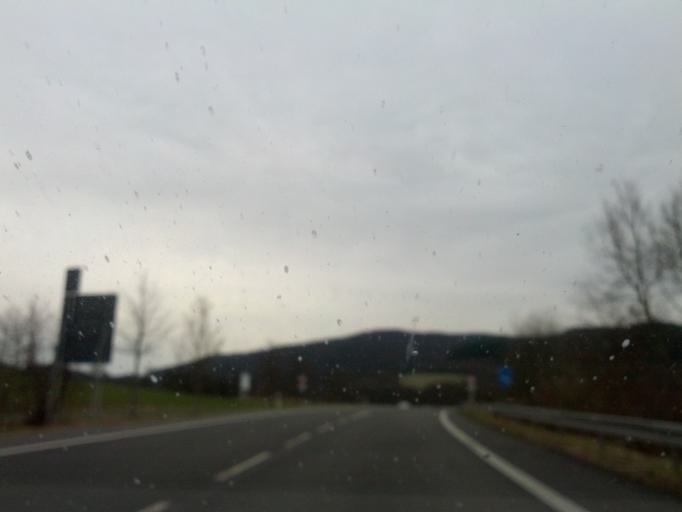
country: DE
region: Hesse
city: Witzenhausen
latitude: 51.3483
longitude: 9.8850
